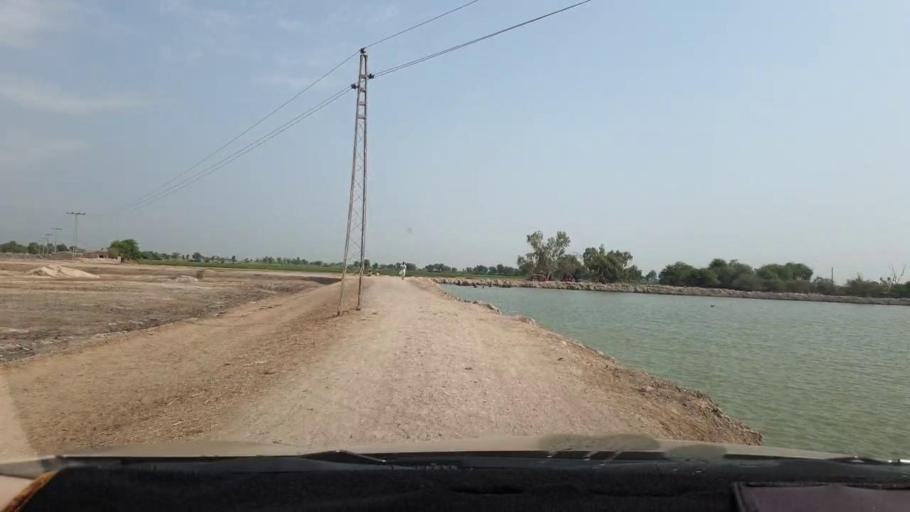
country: PK
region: Sindh
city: Larkana
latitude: 27.6696
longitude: 68.2222
